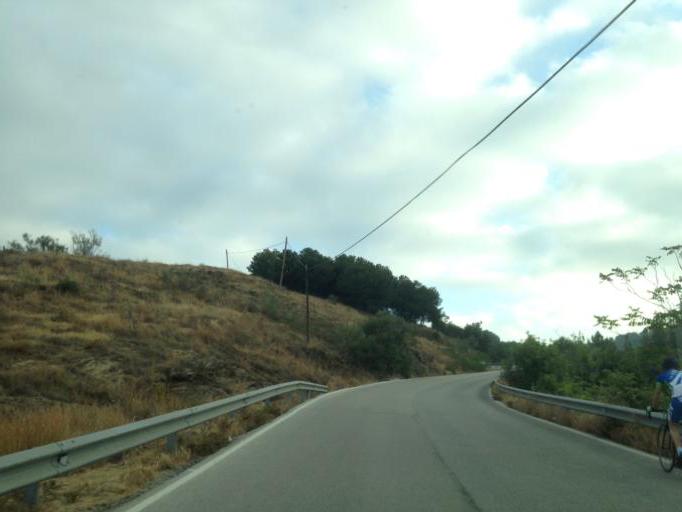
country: ES
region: Andalusia
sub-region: Provincia de Malaga
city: Malaga
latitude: 36.7545
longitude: -4.4082
